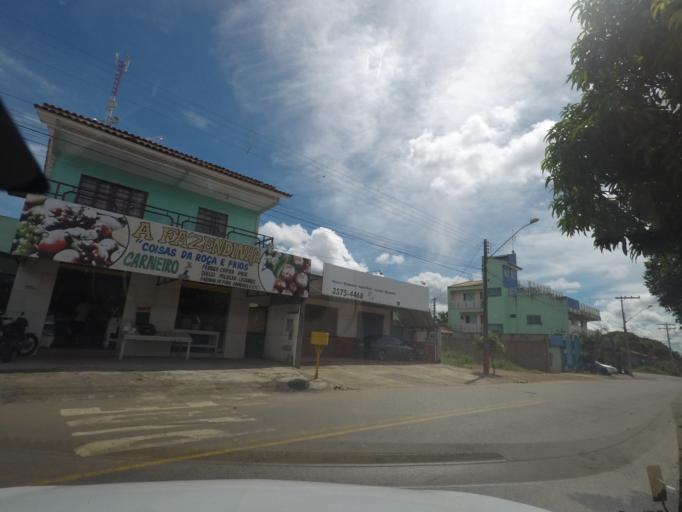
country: BR
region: Goias
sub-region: Goiania
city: Goiania
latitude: -16.7553
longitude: -49.3492
